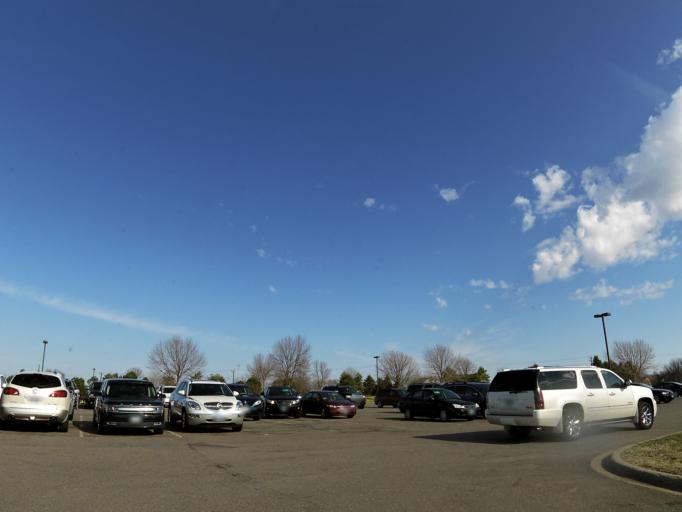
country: US
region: Minnesota
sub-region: Washington County
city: Woodbury
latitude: 44.8896
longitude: -92.9001
